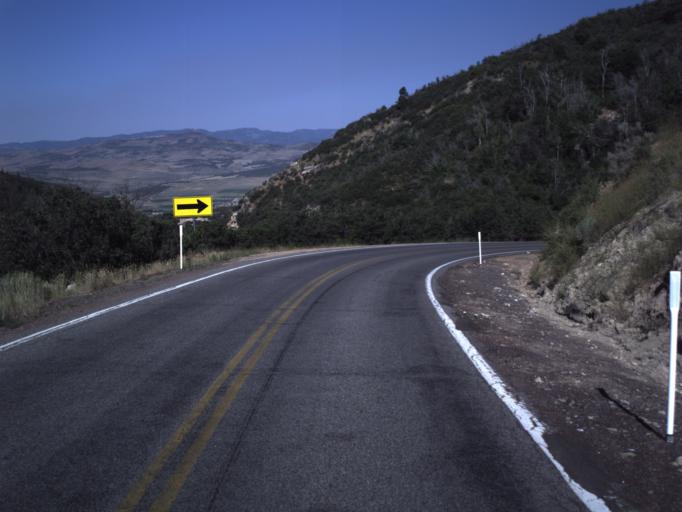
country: US
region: Utah
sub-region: Sanpete County
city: Fairview
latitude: 39.6493
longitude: -111.3874
